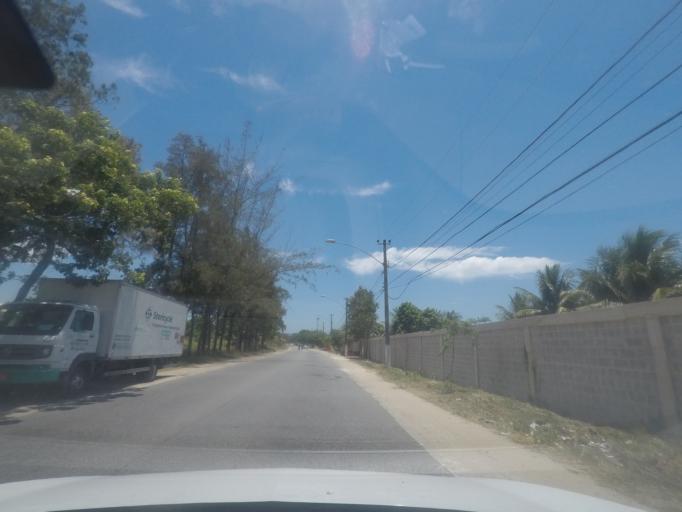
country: BR
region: Rio de Janeiro
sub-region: Itaguai
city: Itaguai
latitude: -22.9033
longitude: -43.6918
